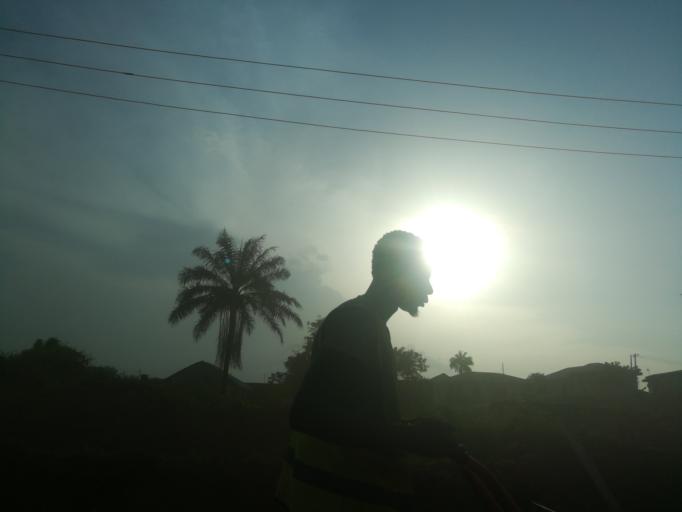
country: NG
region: Oyo
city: Moniya
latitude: 7.5459
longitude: 3.8955
